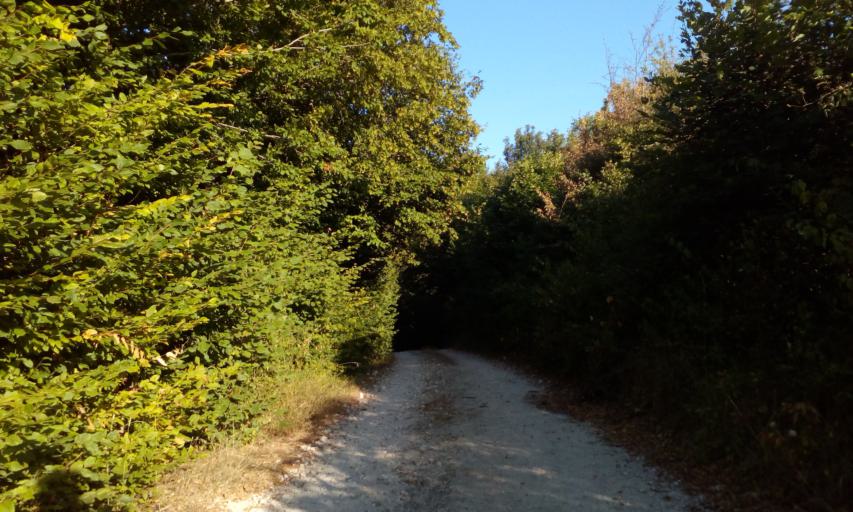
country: FR
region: Lorraine
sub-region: Departement de Meurthe-et-Moselle
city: Pagny-sur-Moselle
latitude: 48.9650
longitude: 5.8822
